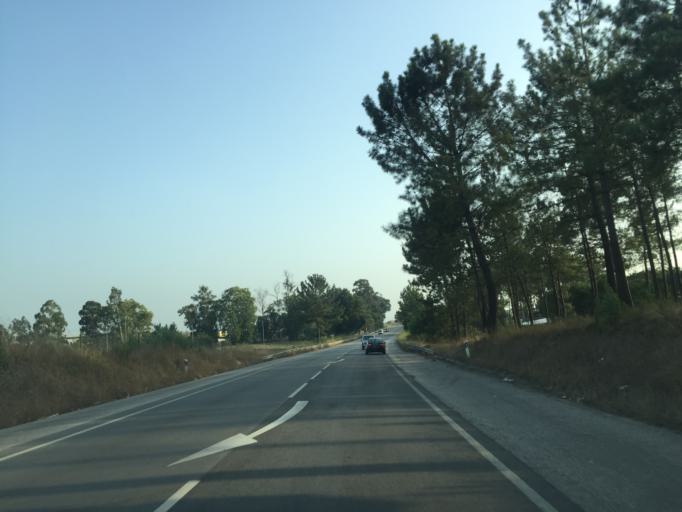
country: PT
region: Leiria
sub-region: Leiria
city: Leiria
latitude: 39.7674
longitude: -8.8153
